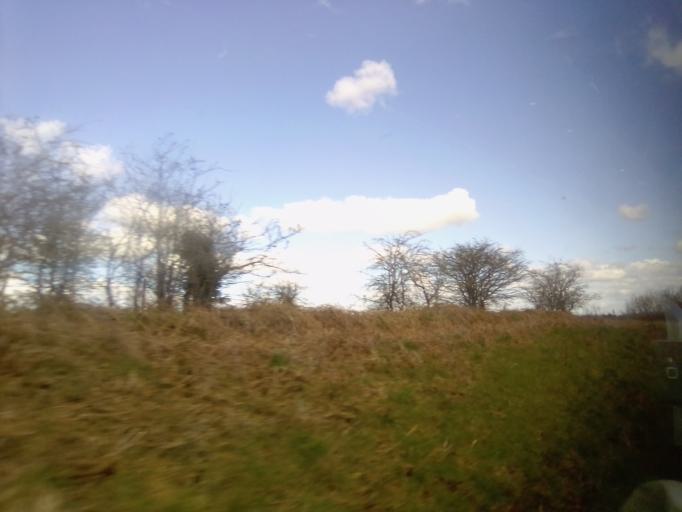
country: IE
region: Munster
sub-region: County Cork
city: Millstreet
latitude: 52.0843
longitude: -9.2031
